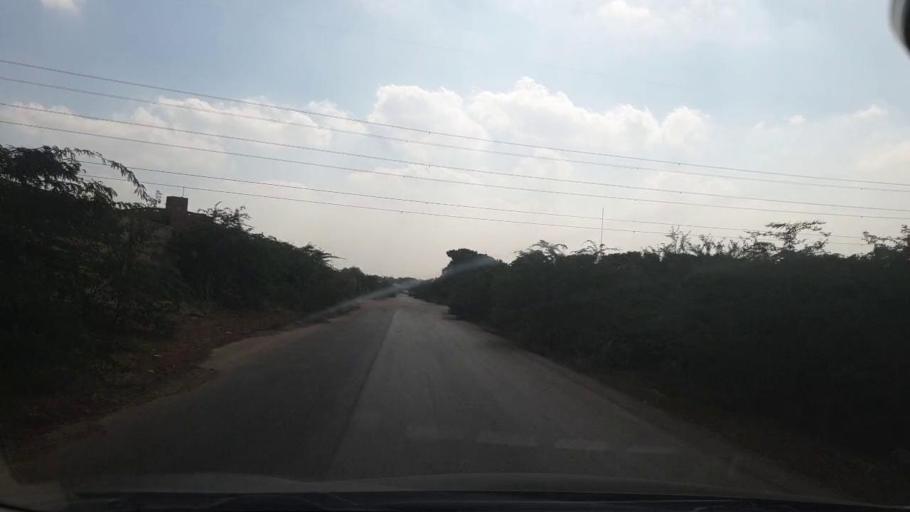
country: PK
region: Sindh
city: Malir Cantonment
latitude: 25.0104
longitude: 67.3547
